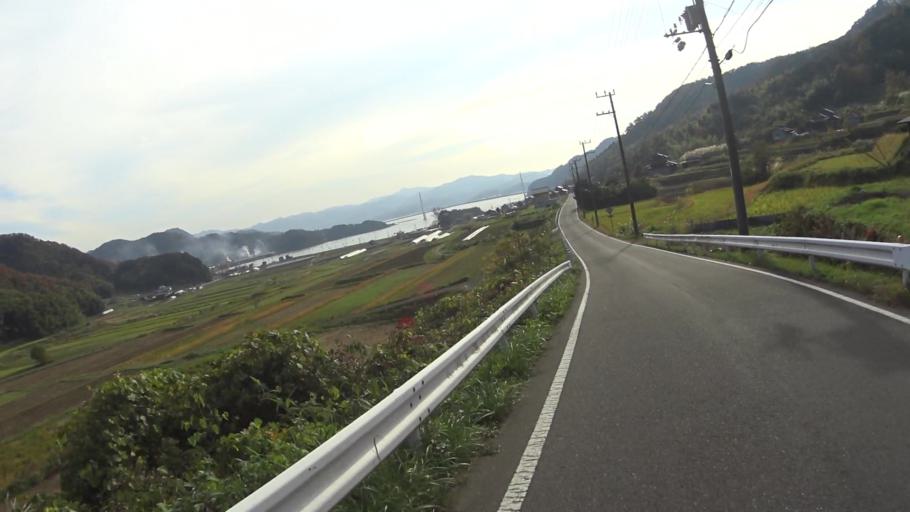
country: JP
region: Kyoto
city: Maizuru
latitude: 35.5268
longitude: 135.3918
